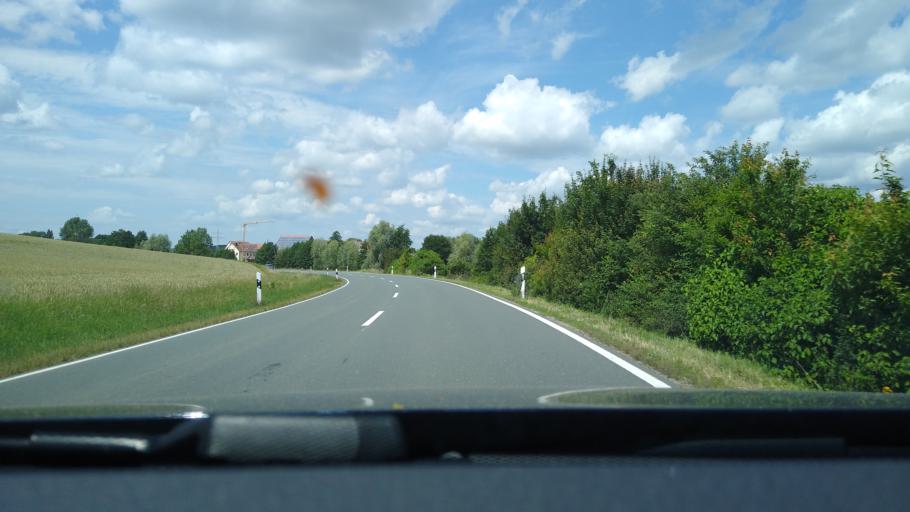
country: DE
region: Bavaria
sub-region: Regierungsbezirk Mittelfranken
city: Obernzenn
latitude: 49.4550
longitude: 10.4990
